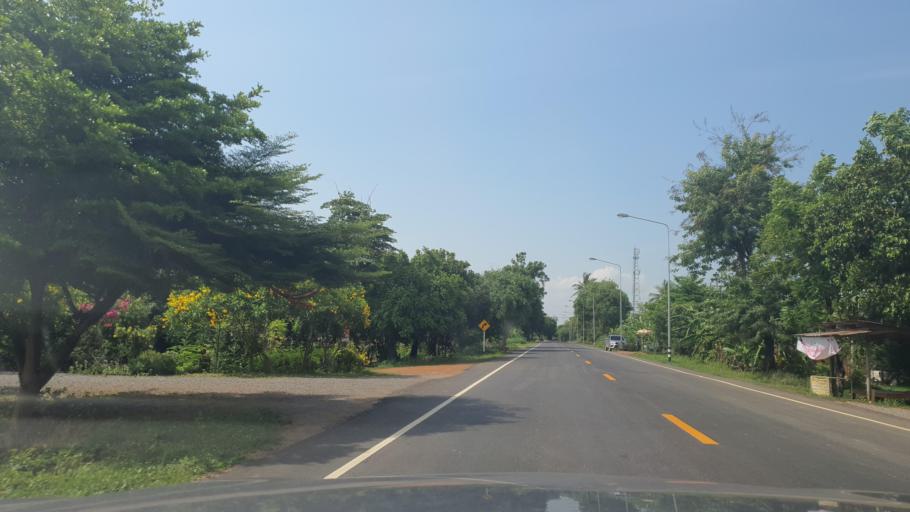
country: TH
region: Sukhothai
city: Si Samrong
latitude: 17.1560
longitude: 99.8269
